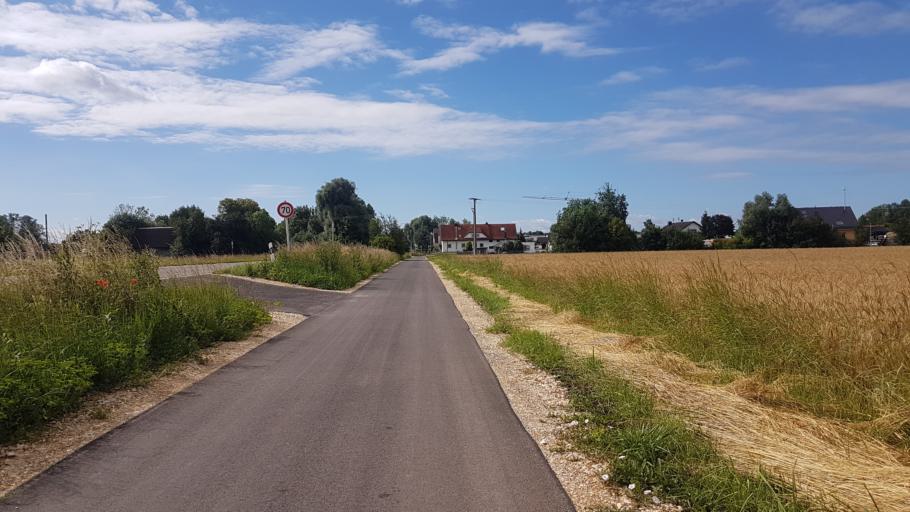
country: DE
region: Bavaria
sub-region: Swabia
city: Guenzburg
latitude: 48.4819
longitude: 10.2588
